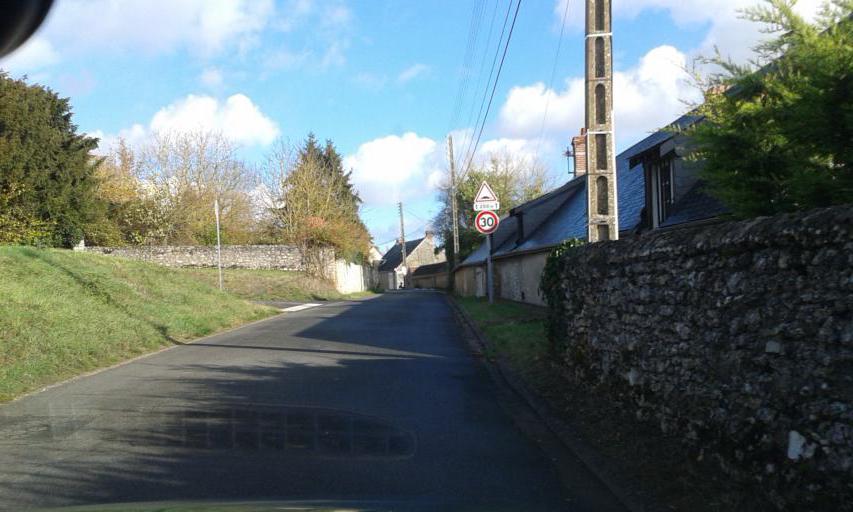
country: FR
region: Centre
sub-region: Departement du Loir-et-Cher
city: Saint-Laurent-Nouan
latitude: 47.7309
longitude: 1.5837
